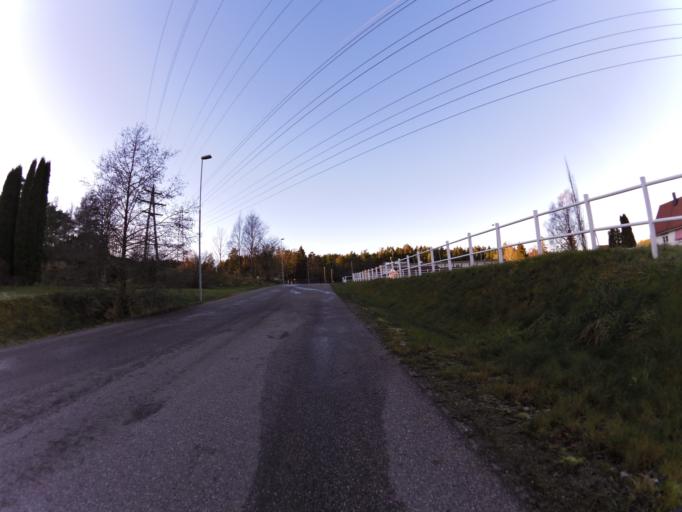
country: NO
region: Ostfold
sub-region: Fredrikstad
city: Fredrikstad
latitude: 59.2439
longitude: 10.9684
